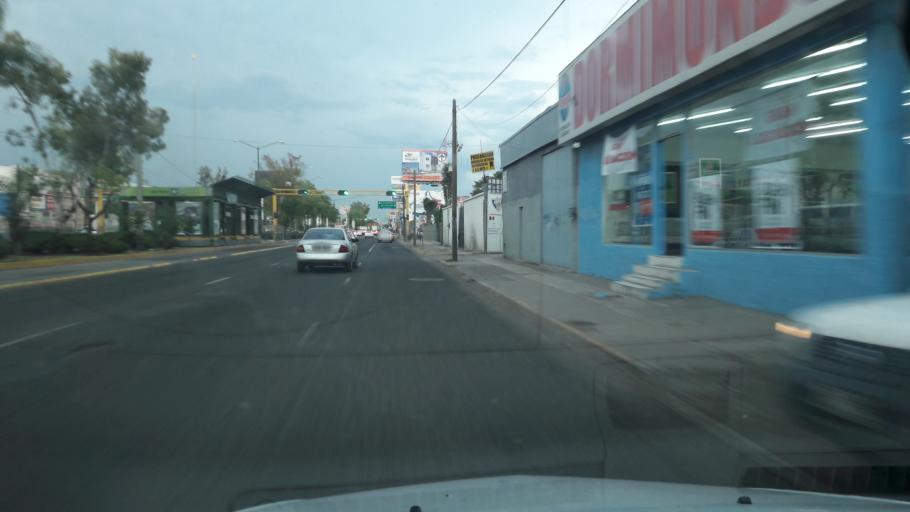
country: MX
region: Guanajuato
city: Leon
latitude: 21.1068
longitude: -101.6419
